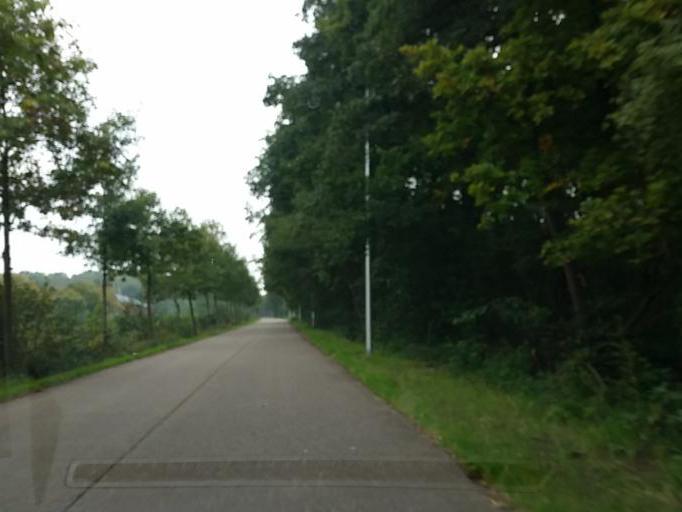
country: BE
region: Flanders
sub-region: Provincie Antwerpen
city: Brasschaat
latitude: 51.3334
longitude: 4.5037
